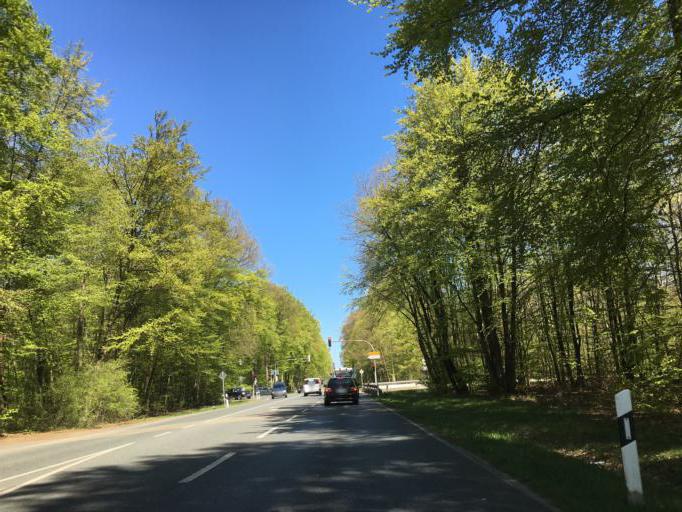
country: DE
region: Hesse
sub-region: Regierungsbezirk Darmstadt
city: Neu Isenburg
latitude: 50.0383
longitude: 8.7105
